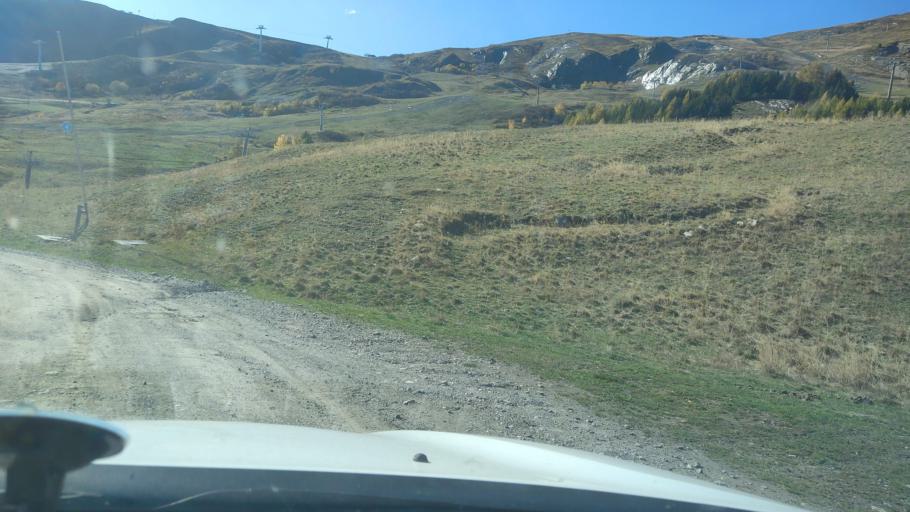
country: FR
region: Rhone-Alpes
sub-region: Departement de la Savoie
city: Saint-Etienne-de-Cuines
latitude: 45.2582
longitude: 6.2515
